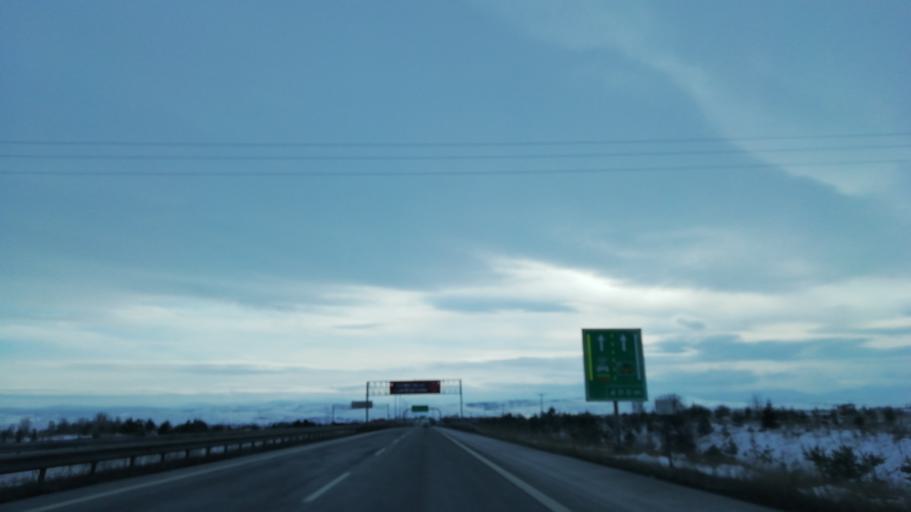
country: TR
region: Bolu
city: Gerede
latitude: 40.7547
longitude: 32.2006
